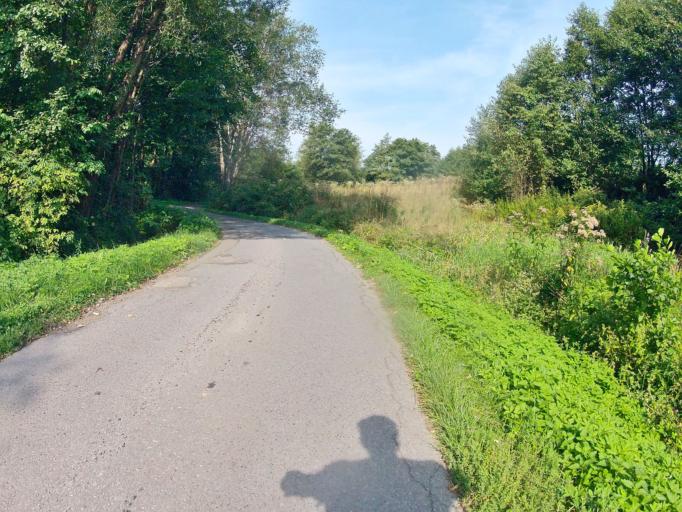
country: PL
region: Subcarpathian Voivodeship
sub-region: Powiat jasielski
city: Brzyska
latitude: 49.7929
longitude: 21.3859
